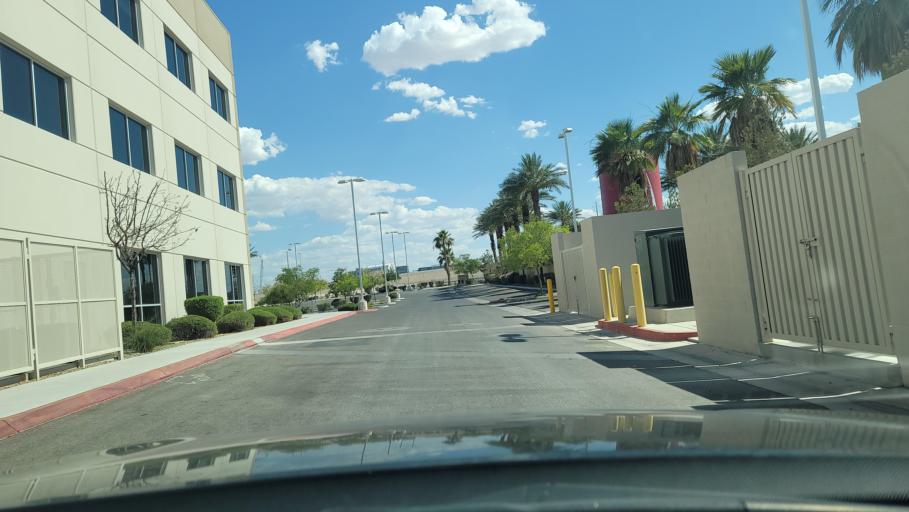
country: US
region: Nevada
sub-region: Clark County
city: Spring Valley
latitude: 36.0716
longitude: -115.2782
